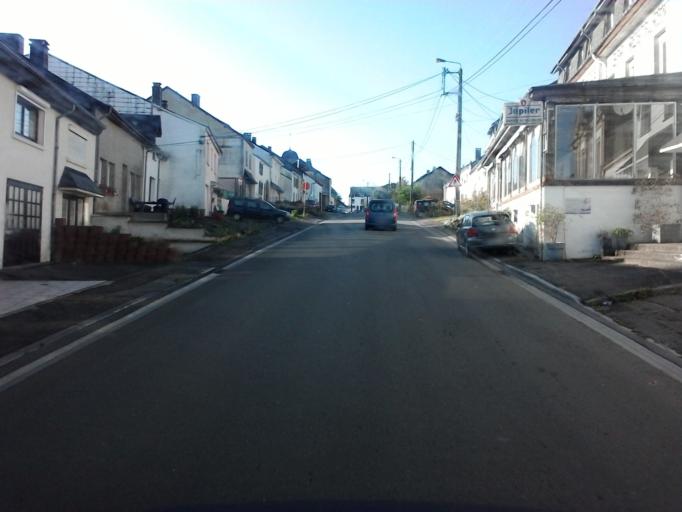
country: BE
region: Wallonia
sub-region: Province du Luxembourg
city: Chiny
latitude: 49.7399
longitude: 5.3421
